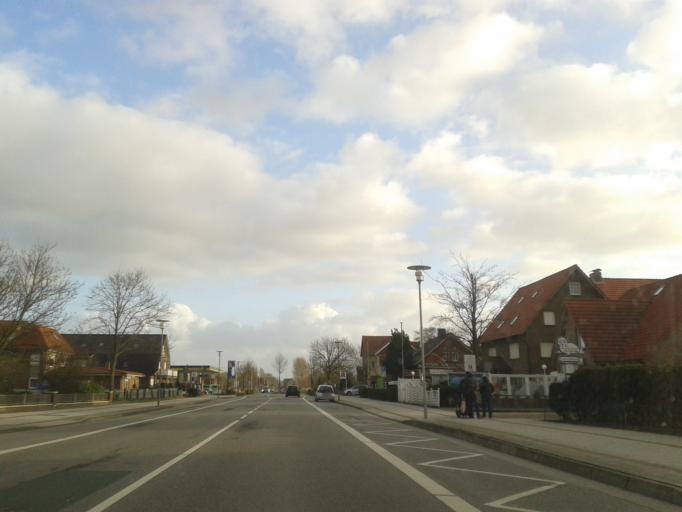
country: DE
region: Lower Saxony
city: Norddeich
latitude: 53.6147
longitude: 7.1647
